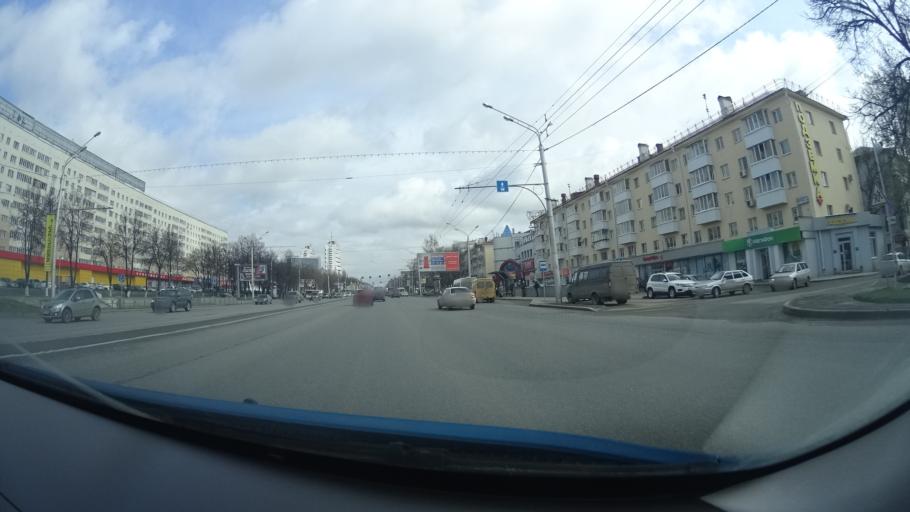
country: RU
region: Bashkortostan
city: Ufa
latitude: 54.7588
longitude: 56.0088
